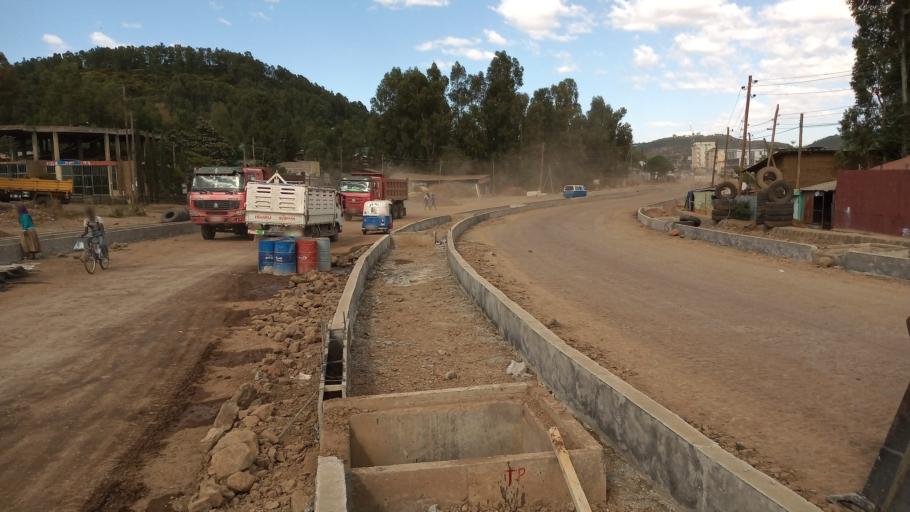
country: ET
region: Amhara
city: Gondar
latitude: 12.5624
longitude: 37.4306
